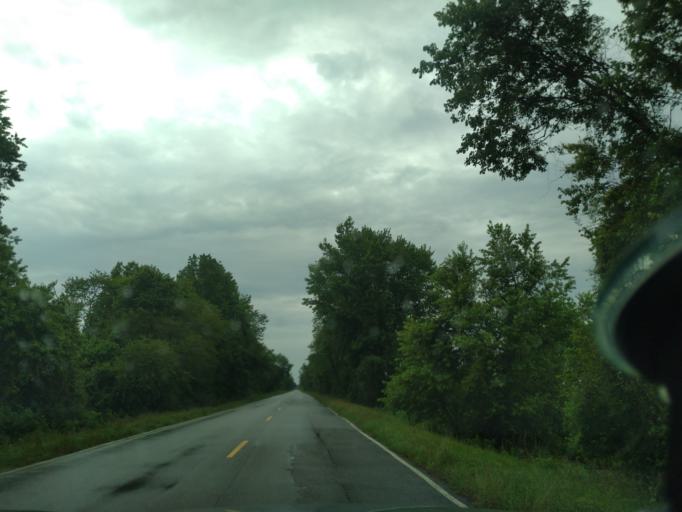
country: US
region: North Carolina
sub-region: Washington County
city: Plymouth
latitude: 35.8401
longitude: -76.5439
